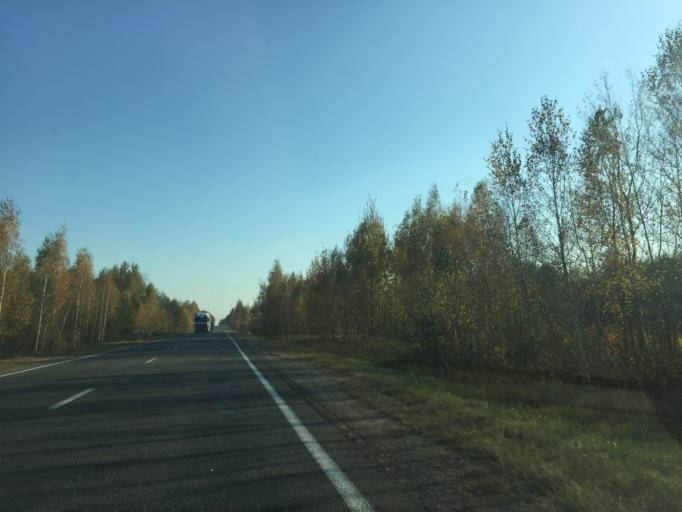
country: BY
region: Gomel
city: Dobrush
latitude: 52.3402
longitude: 31.2326
